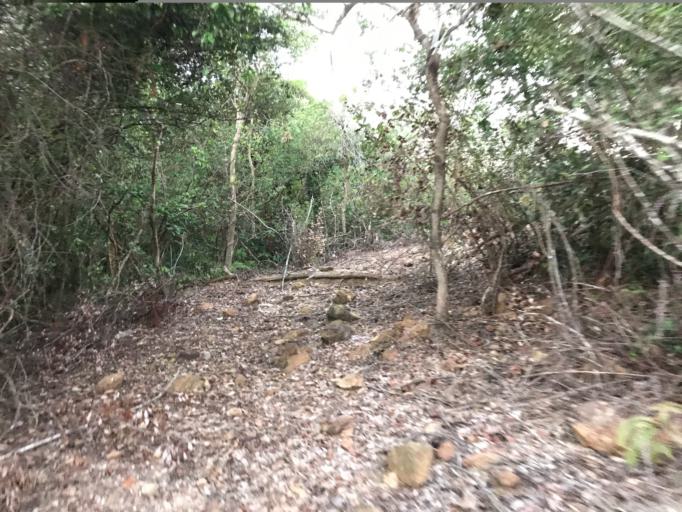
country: HK
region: Tai Po
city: Tai Po
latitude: 22.4720
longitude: 114.1455
